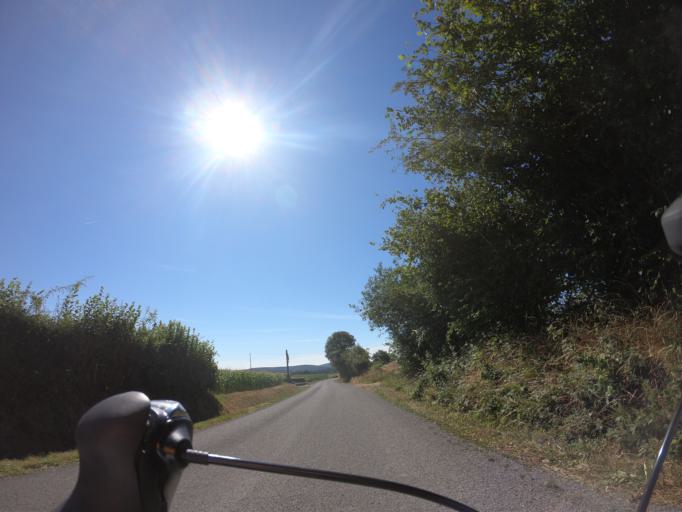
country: FR
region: Lower Normandy
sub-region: Departement de l'Orne
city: Saint-Denis-sur-Sarthon
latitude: 48.5353
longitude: -0.0962
